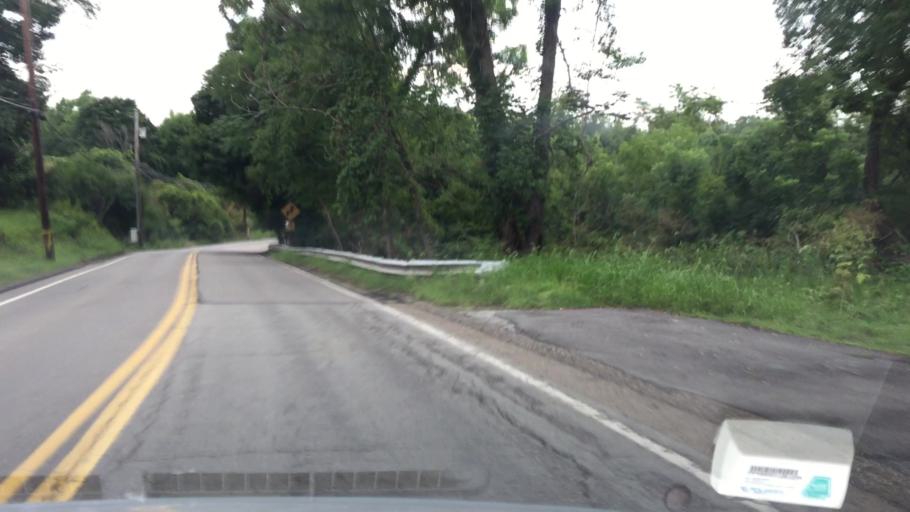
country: US
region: Pennsylvania
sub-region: Allegheny County
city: Glenshaw
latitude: 40.5180
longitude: -79.9818
